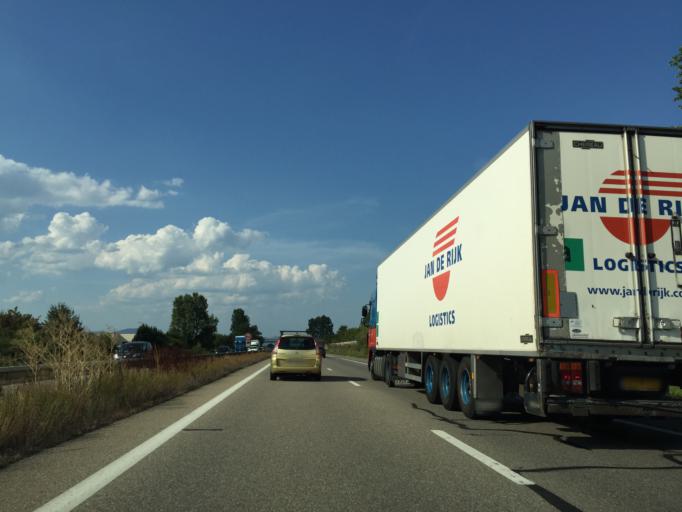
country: FR
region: Alsace
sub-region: Departement du Haut-Rhin
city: Houssen
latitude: 48.1040
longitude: 7.3826
